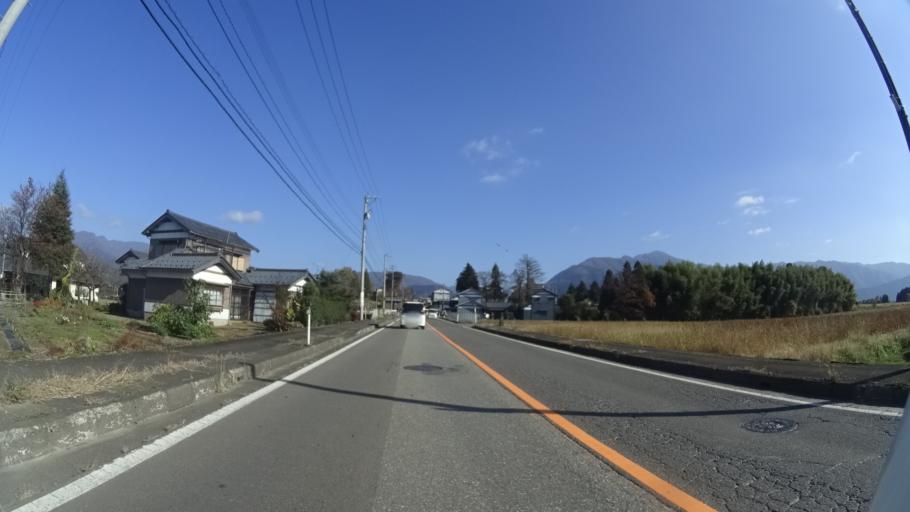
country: JP
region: Fukui
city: Ono
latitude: 35.9796
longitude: 136.5271
